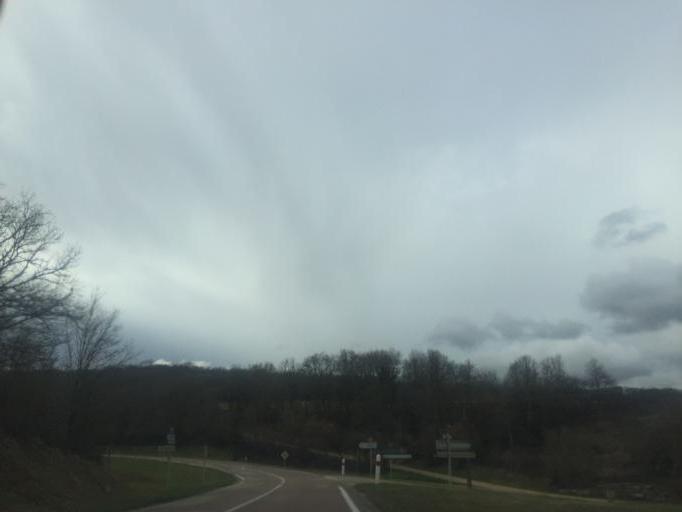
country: FR
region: Bourgogne
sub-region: Departement de la Nievre
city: Clamecy
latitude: 47.4576
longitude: 3.6493
